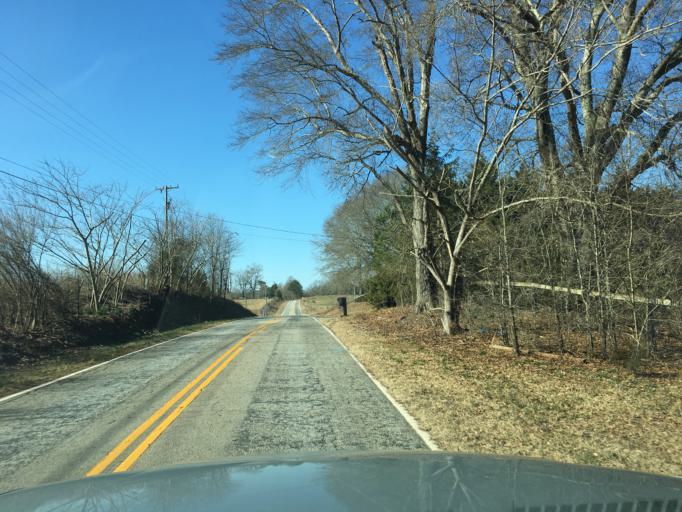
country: US
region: South Carolina
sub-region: Pickens County
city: Pickens
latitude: 34.8580
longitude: -82.7552
